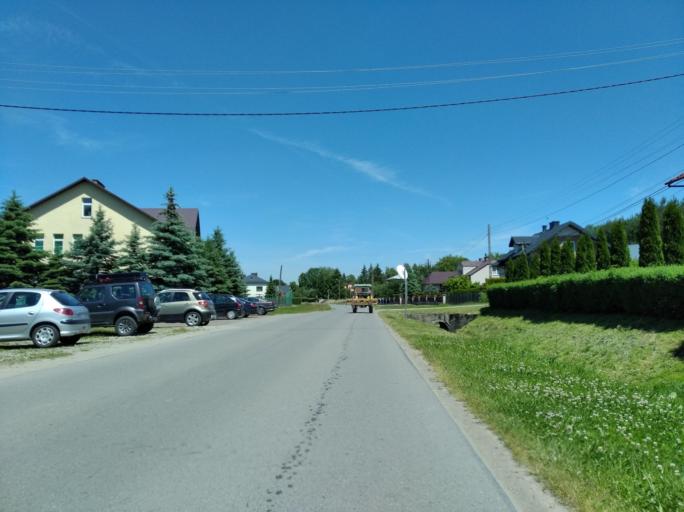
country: PL
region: Subcarpathian Voivodeship
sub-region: Powiat jasielski
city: Tarnowiec
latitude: 49.6946
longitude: 21.5536
